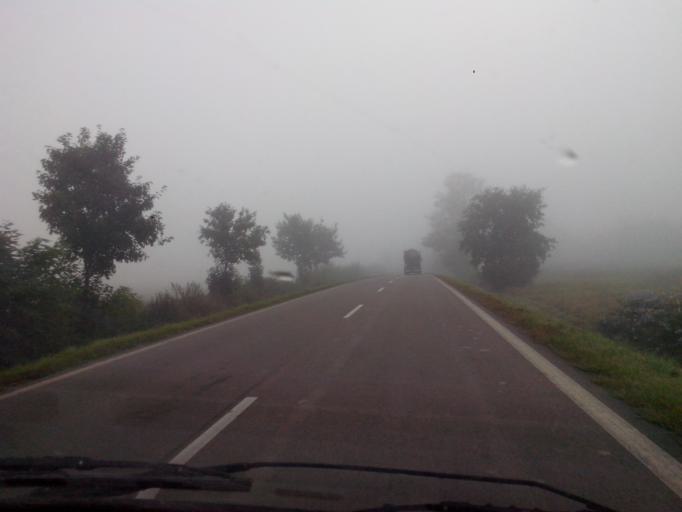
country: PL
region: Subcarpathian Voivodeship
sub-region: Powiat przemyski
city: Krasiczyn
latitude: 49.7993
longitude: 22.6419
